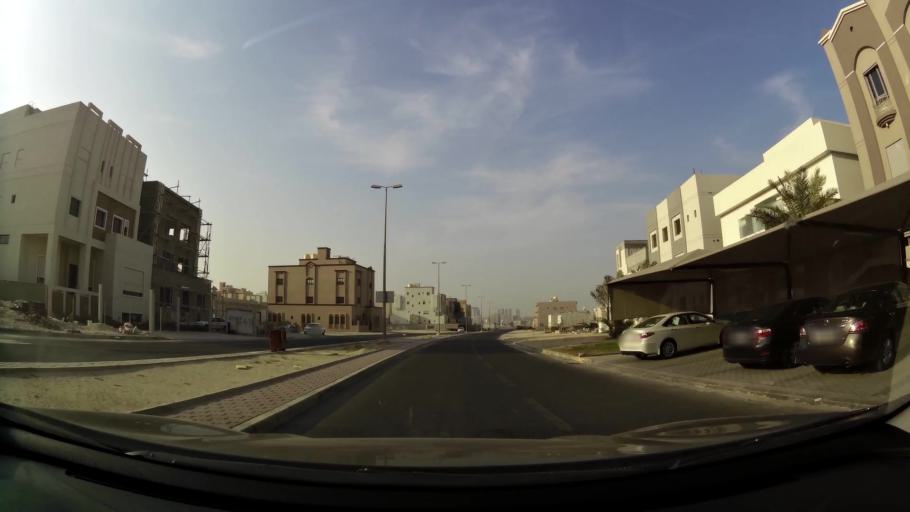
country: KW
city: Al Funaytis
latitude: 29.2326
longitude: 48.0888
